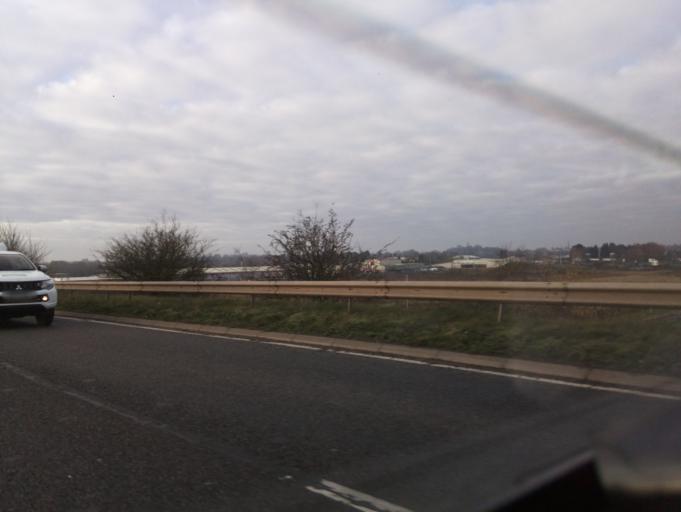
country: GB
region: England
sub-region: Staffordshire
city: Whittington
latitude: 52.6867
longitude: -1.7917
